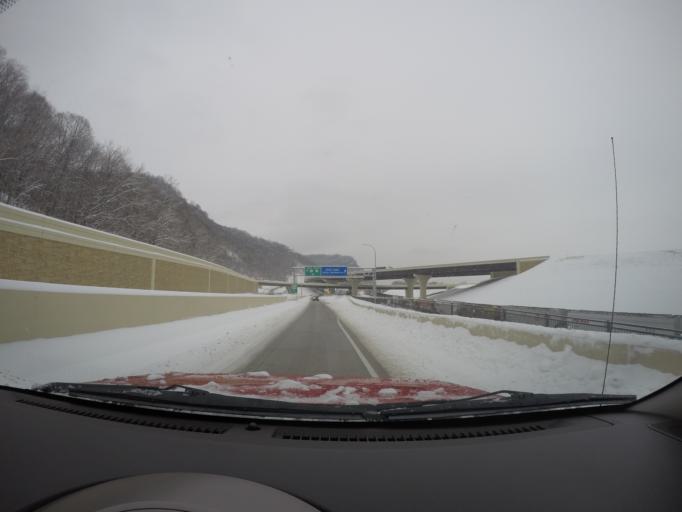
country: US
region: Minnesota
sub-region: Houston County
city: La Crescent
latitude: 43.8568
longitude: -91.3051
